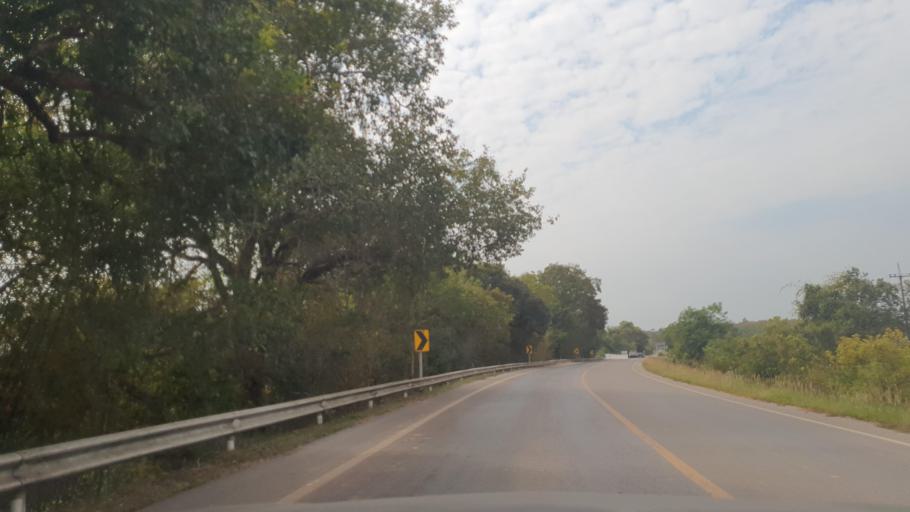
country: TH
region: Changwat Bueng Kan
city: Bung Khla
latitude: 18.2832
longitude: 103.8826
